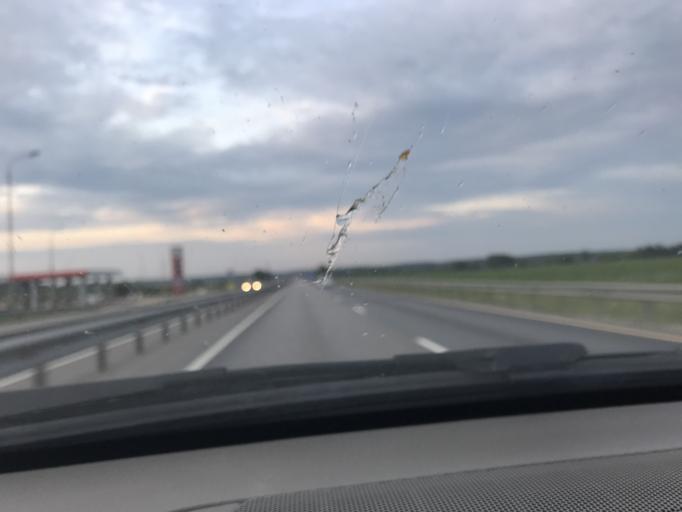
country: RU
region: Kaluga
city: Obninsk
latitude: 55.0368
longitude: 36.5880
